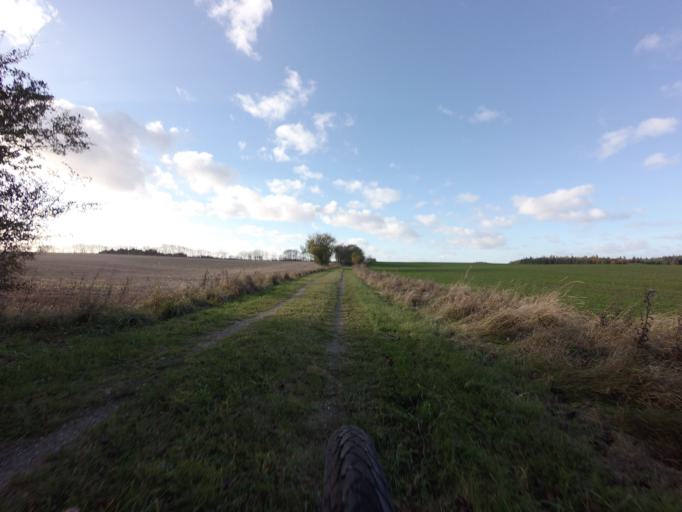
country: DK
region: Central Jutland
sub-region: Syddjurs Kommune
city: Ryomgard
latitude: 56.4911
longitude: 10.6770
